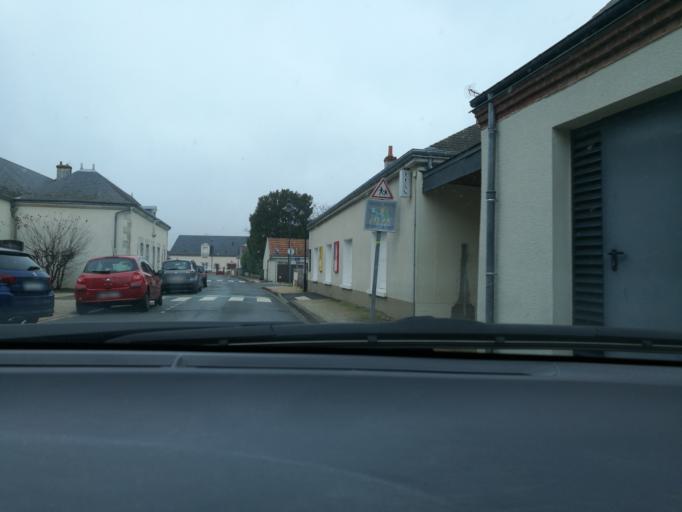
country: FR
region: Centre
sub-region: Departement du Loiret
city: Semoy
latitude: 47.9323
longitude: 1.9501
